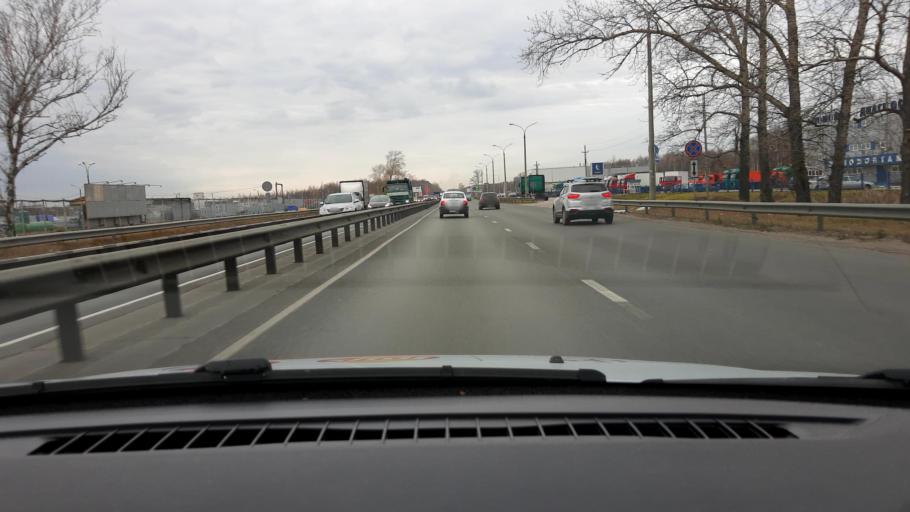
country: RU
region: Nizjnij Novgorod
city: Gorbatovka
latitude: 56.3095
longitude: 43.7939
